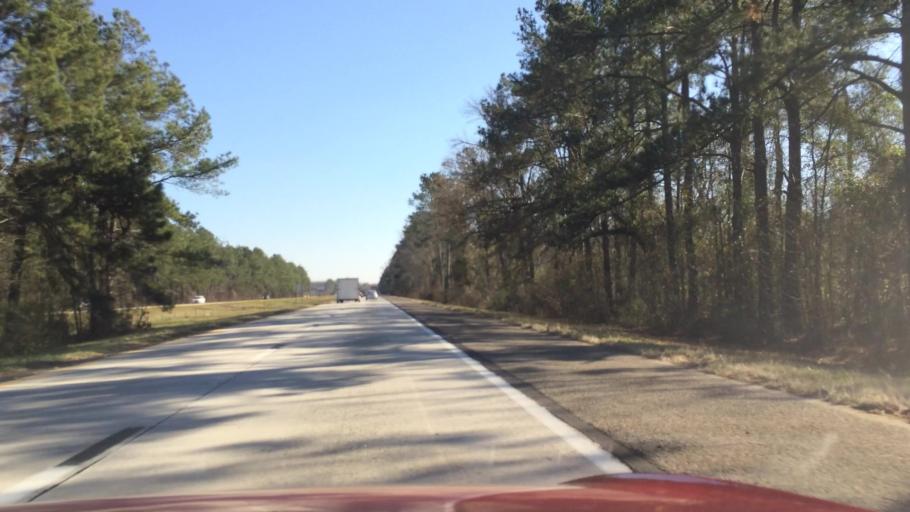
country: US
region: South Carolina
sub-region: Orangeburg County
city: Holly Hill
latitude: 33.2530
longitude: -80.4710
